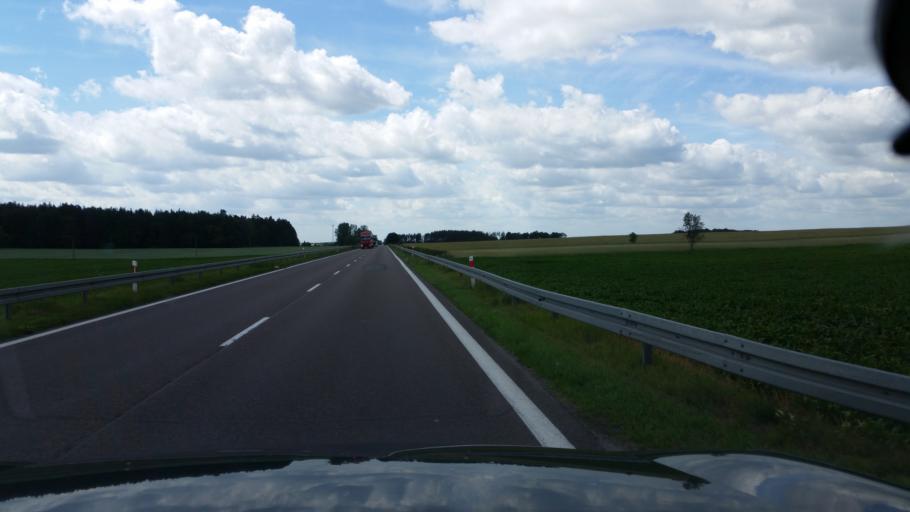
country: PL
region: Podlasie
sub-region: Powiat grajewski
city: Szczuczyn
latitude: 53.4796
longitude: 22.2133
